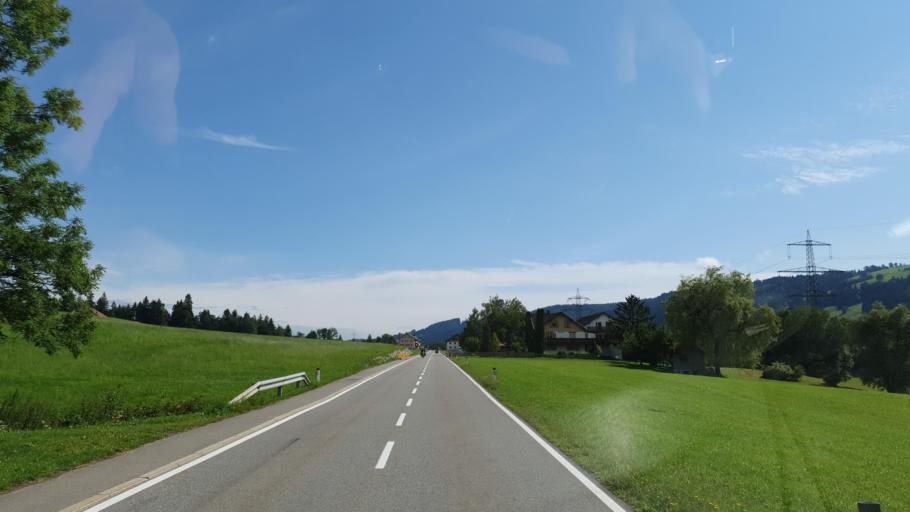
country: AT
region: Vorarlberg
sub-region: Politischer Bezirk Bregenz
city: Doren
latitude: 47.5261
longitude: 9.8584
